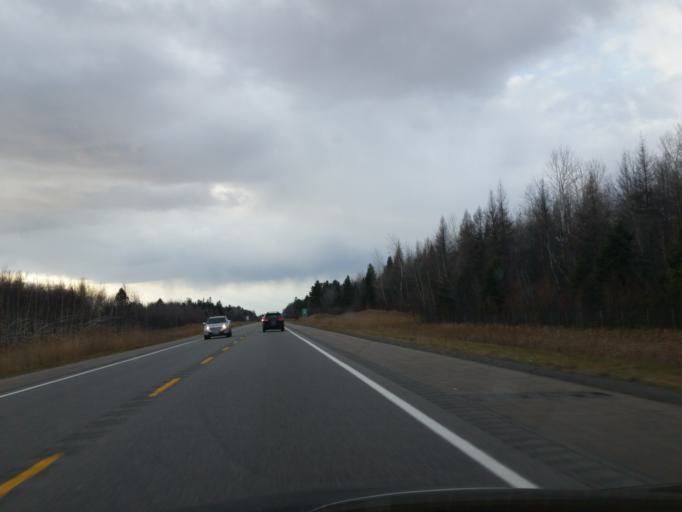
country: CA
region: Quebec
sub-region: Laurentides
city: Lachute
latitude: 45.6420
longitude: -74.2772
